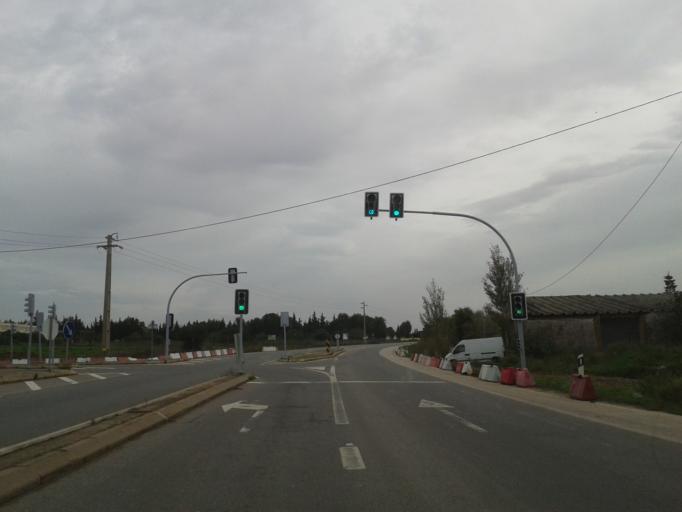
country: PT
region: Faro
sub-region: Lagos
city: Lagos
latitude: 37.0993
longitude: -8.7370
